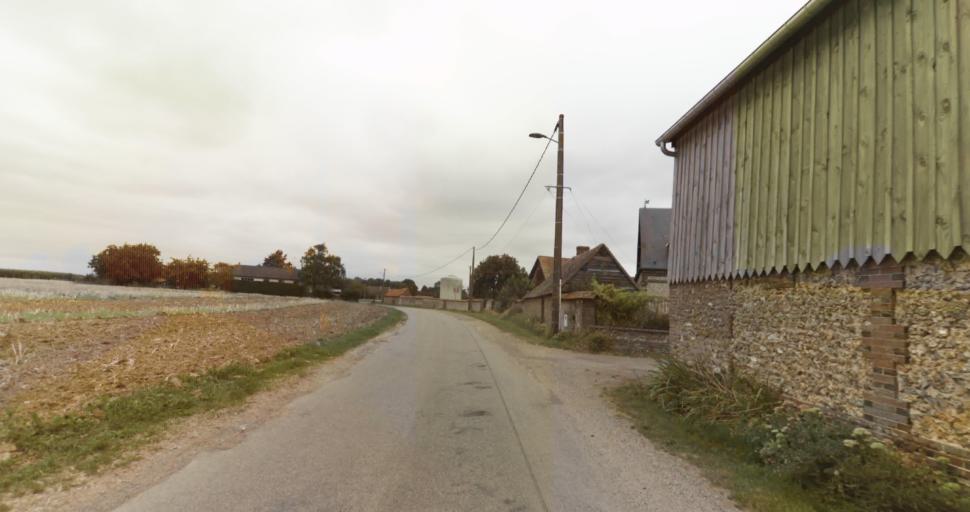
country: FR
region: Haute-Normandie
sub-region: Departement de l'Eure
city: La Couture-Boussey
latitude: 48.9267
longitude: 1.3264
